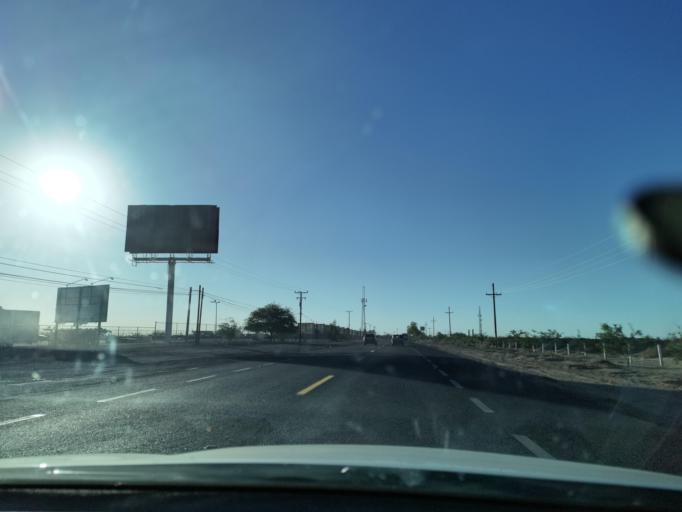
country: MX
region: Baja California
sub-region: Mexicali
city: Islas Agrarias Grupo A
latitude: 32.6310
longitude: -115.2611
